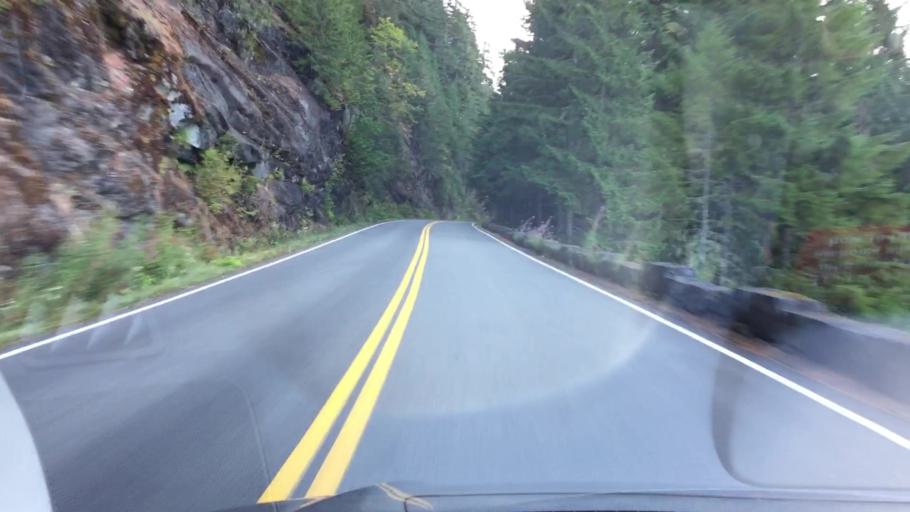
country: US
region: Washington
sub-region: Pierce County
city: Buckley
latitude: 46.7306
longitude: -121.5835
